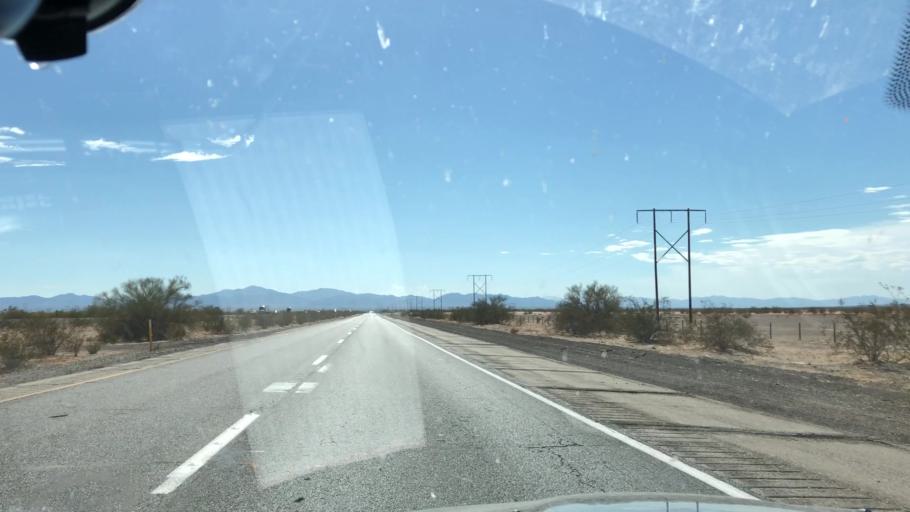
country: US
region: California
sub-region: Riverside County
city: Mesa Verde
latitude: 33.6063
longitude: -114.9498
